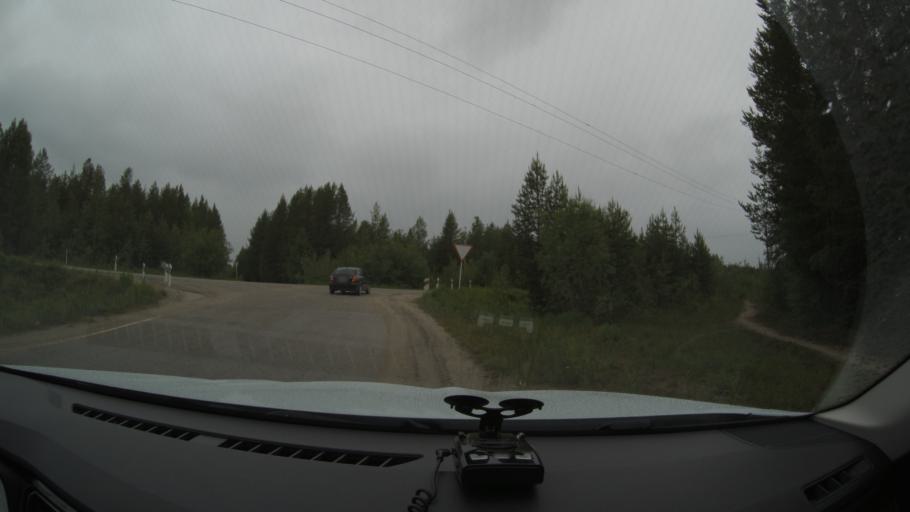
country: RU
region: Komi Republic
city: Kozhva
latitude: 65.1098
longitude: 57.0117
